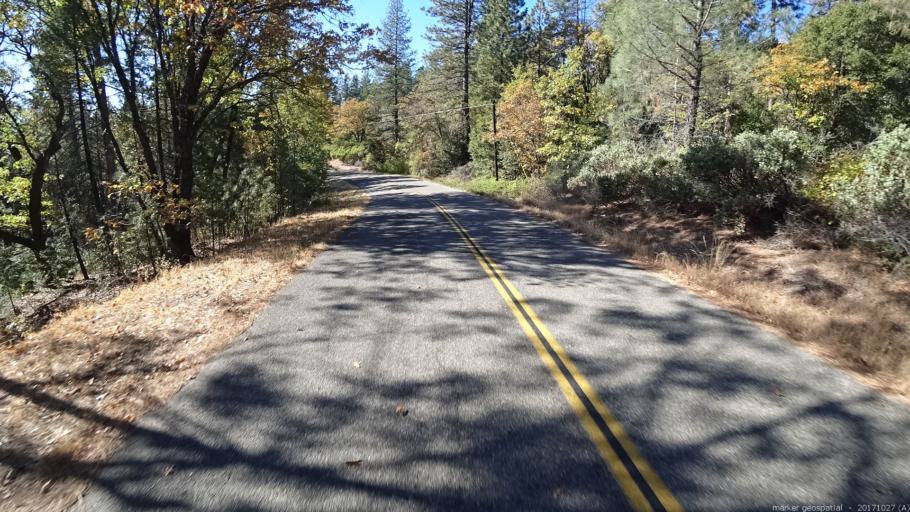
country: US
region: California
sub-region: Shasta County
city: Shingletown
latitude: 40.6864
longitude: -121.8932
